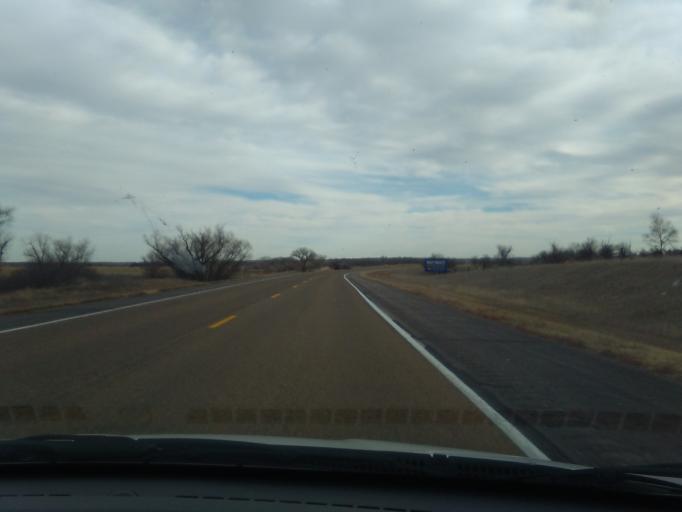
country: US
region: Colorado
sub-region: Yuma County
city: Wray
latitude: 40.0368
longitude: -101.9779
